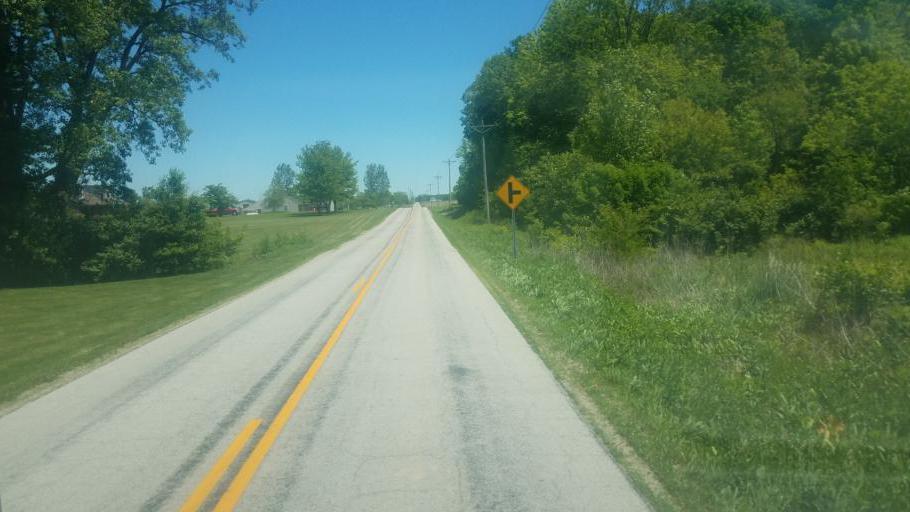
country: US
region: Ohio
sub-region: Miami County
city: Covington
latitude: 40.2270
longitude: -84.3461
